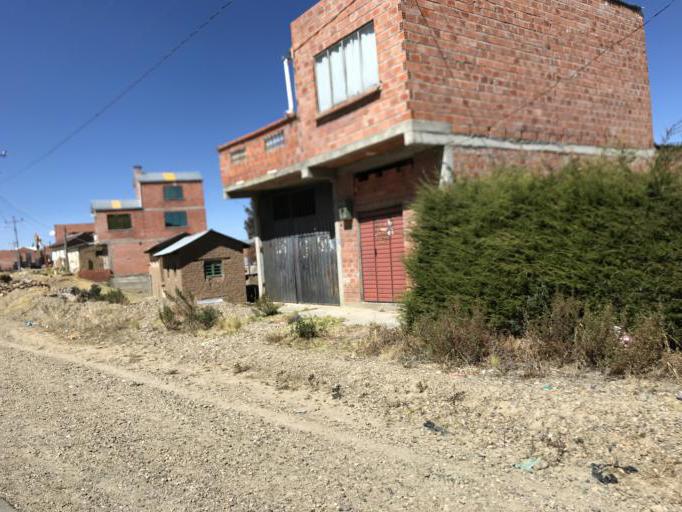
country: BO
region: La Paz
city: Huatajata
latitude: -16.2148
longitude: -68.6709
